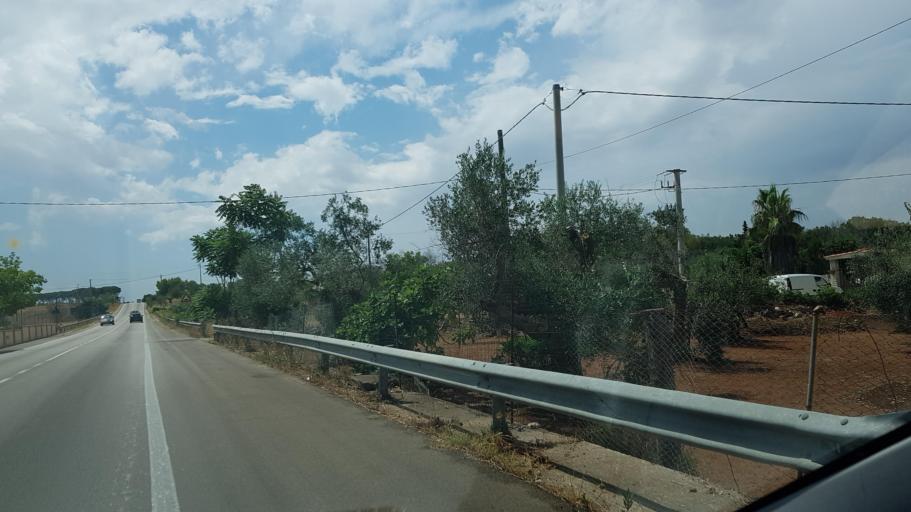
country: IT
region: Apulia
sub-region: Provincia di Lecce
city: Ruffano
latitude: 39.9613
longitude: 18.2568
